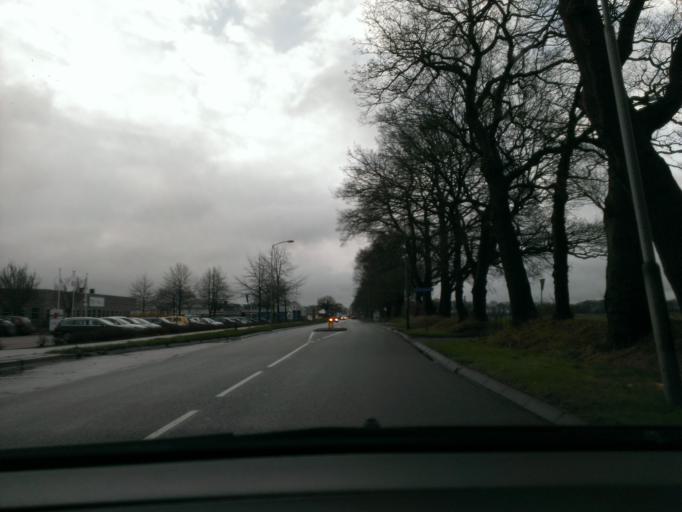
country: NL
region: Drenthe
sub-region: Gemeente Emmen
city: Emmen
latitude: 52.7572
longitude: 6.9130
